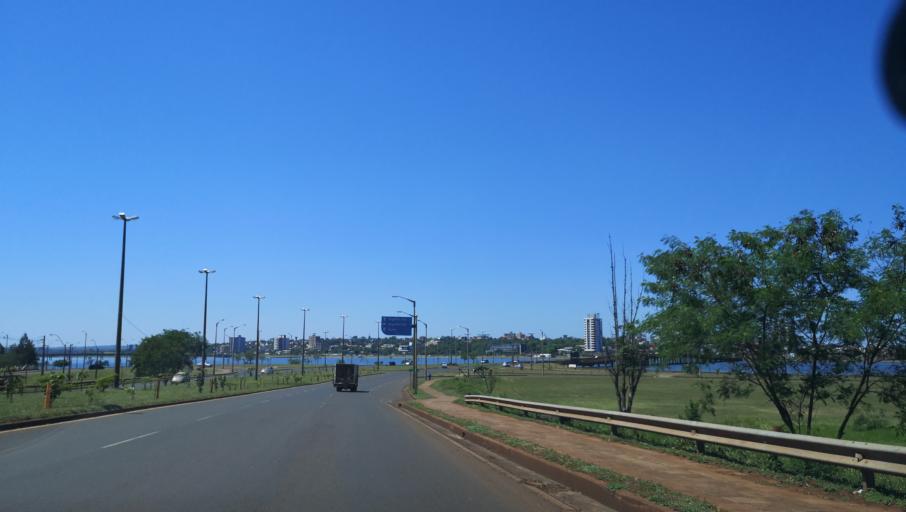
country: PY
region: Itapua
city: Encarnacion
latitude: -27.3139
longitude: -55.8773
